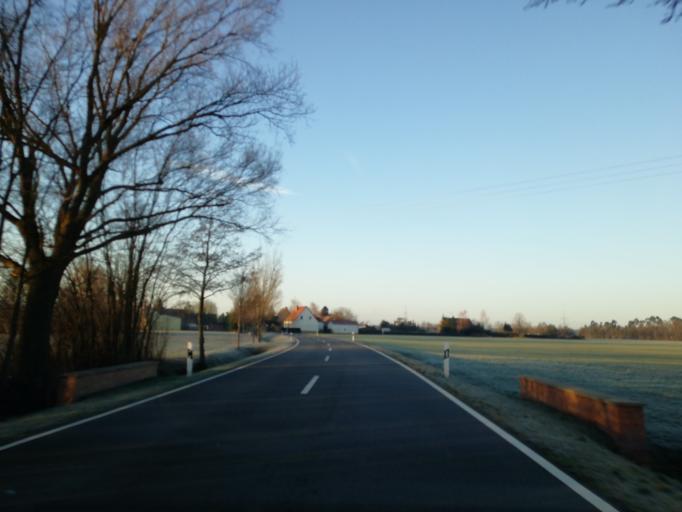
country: DE
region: Brandenburg
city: Finsterwalde
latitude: 51.6659
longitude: 13.7143
